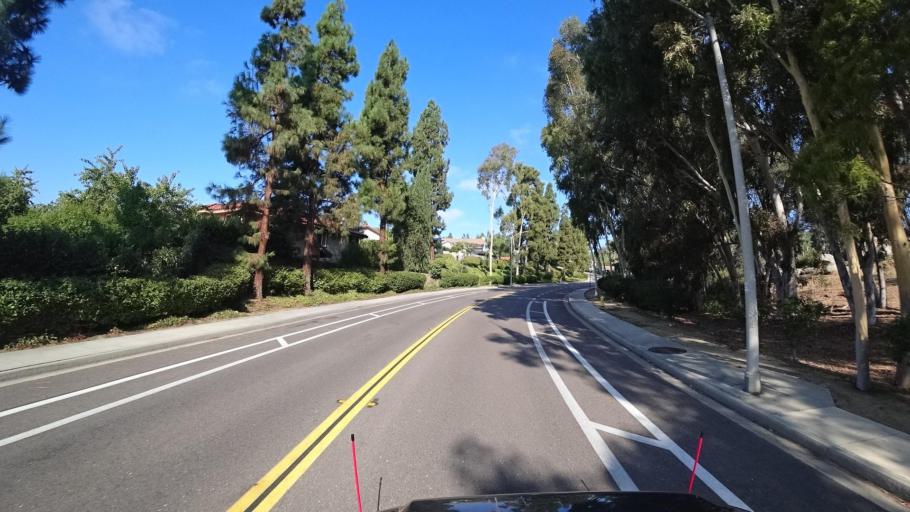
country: US
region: California
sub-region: San Diego County
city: Vista
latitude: 33.1706
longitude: -117.2292
